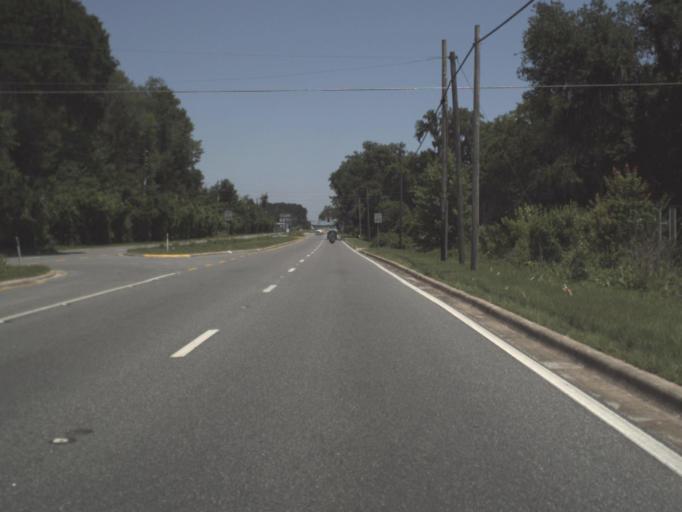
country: US
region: Florida
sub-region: Columbia County
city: Watertown
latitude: 30.1862
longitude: -82.6028
